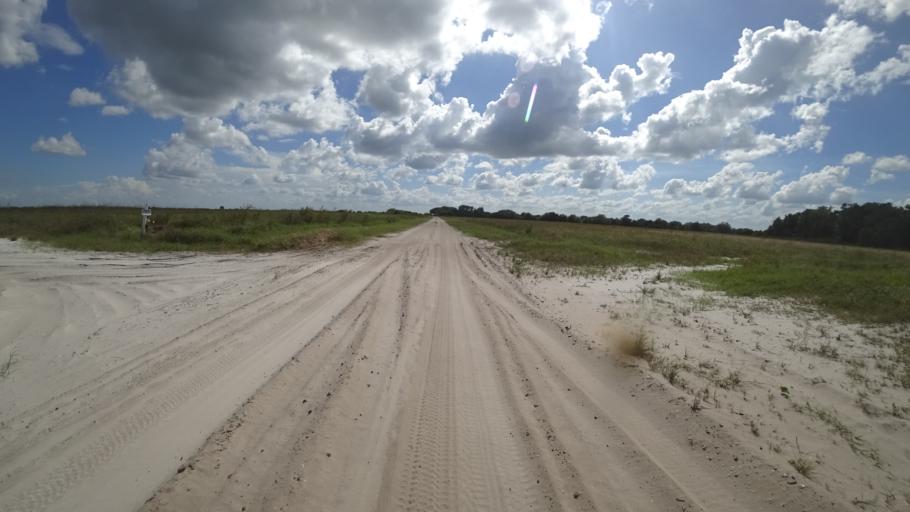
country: US
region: Florida
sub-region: DeSoto County
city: Arcadia
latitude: 27.3427
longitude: -82.1050
